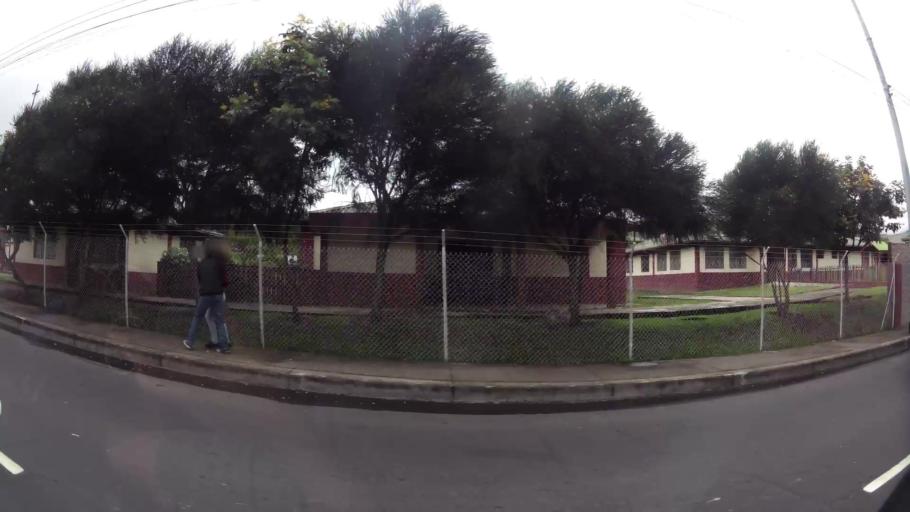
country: EC
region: Pichincha
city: Quito
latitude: -0.2847
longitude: -78.5499
